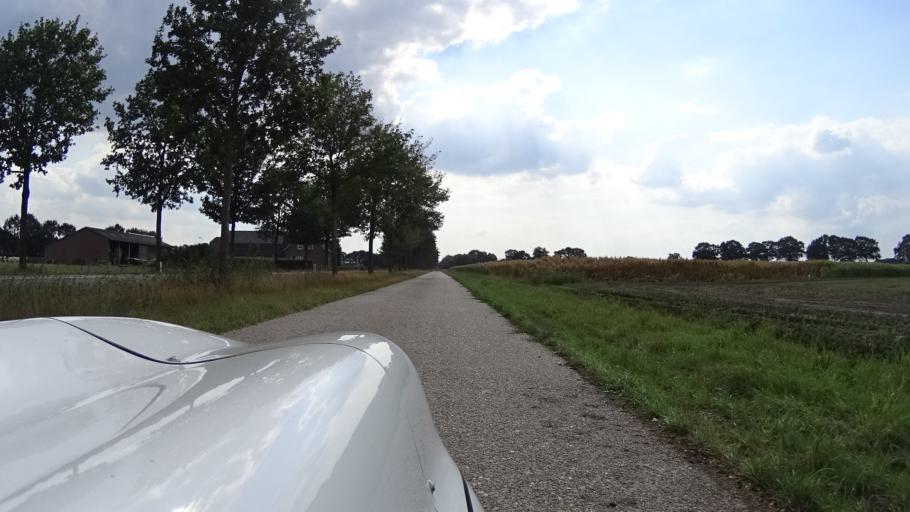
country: NL
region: North Brabant
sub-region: Gemeente Sint Anthonis
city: Sint Anthonis
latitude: 51.6093
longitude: 5.8591
